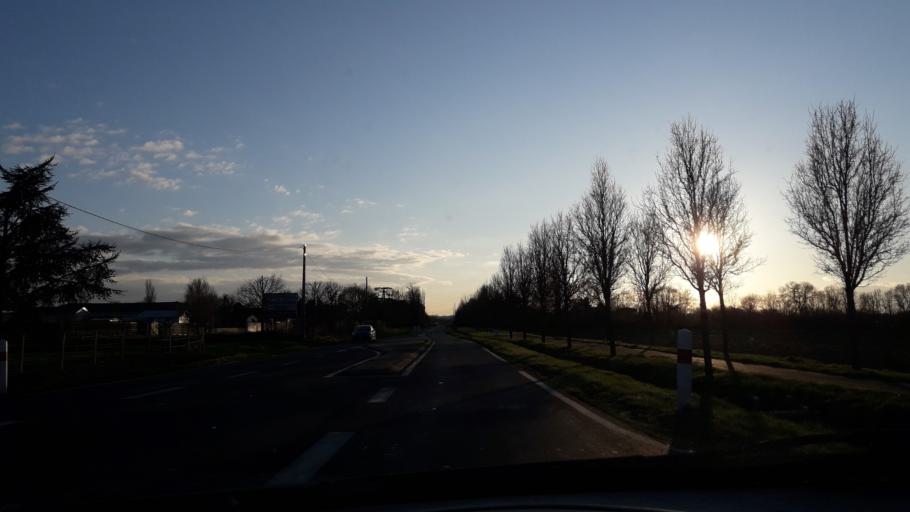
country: FR
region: Midi-Pyrenees
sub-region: Departement de la Haute-Garonne
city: Levignac
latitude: 43.6463
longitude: 1.1653
